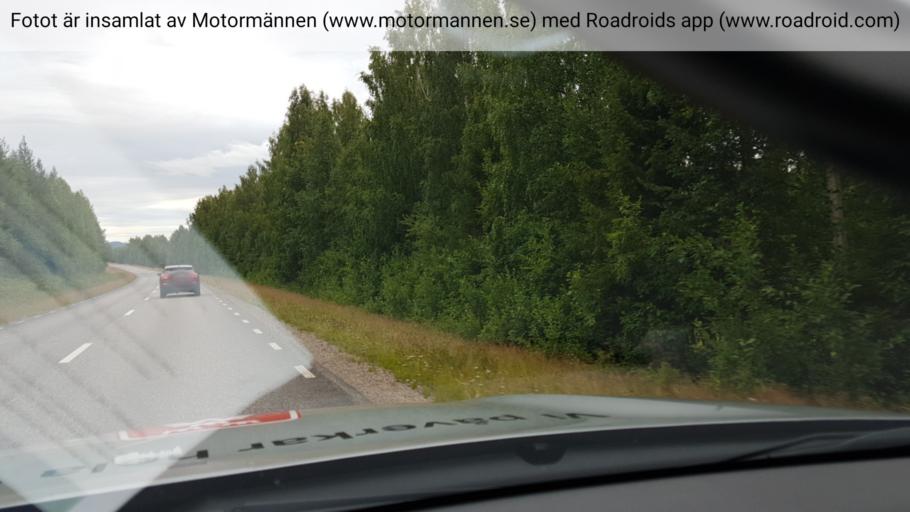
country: SE
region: Norrbotten
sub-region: Overkalix Kommun
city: OEverkalix
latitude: 66.5448
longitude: 22.7544
